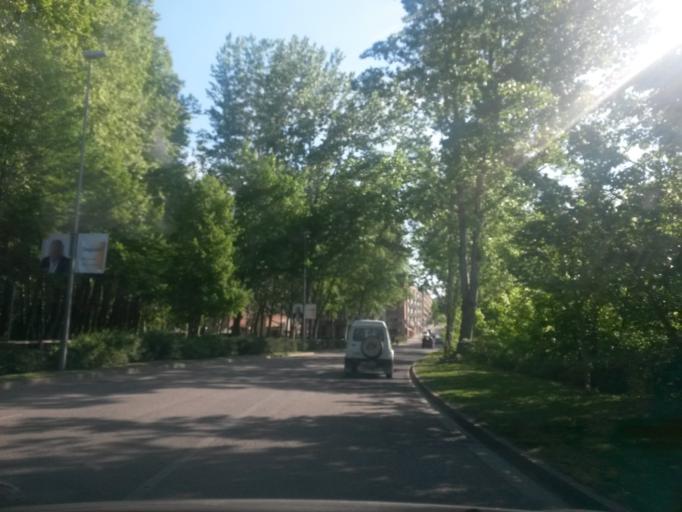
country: ES
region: Catalonia
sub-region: Provincia de Girona
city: Olot
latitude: 42.1745
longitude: 2.4881
